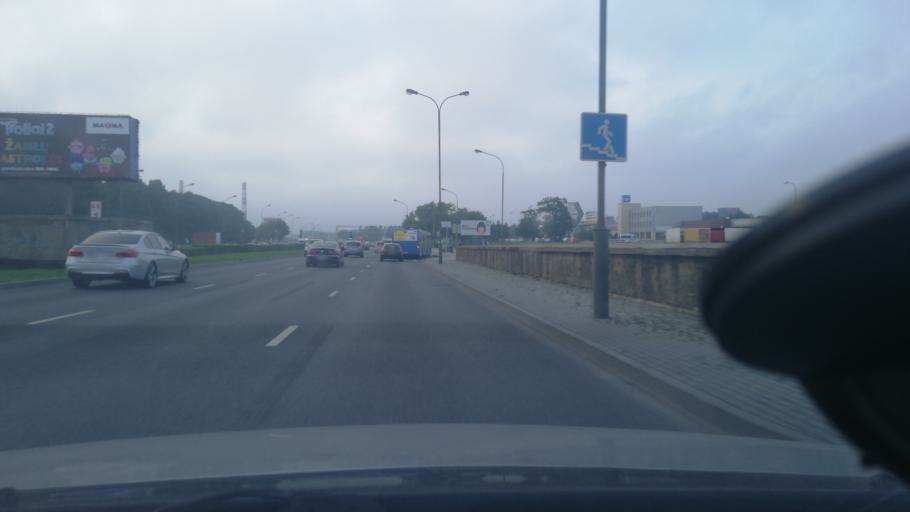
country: LT
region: Klaipedos apskritis
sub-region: Klaipeda
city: Klaipeda
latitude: 55.6884
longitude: 21.1819
